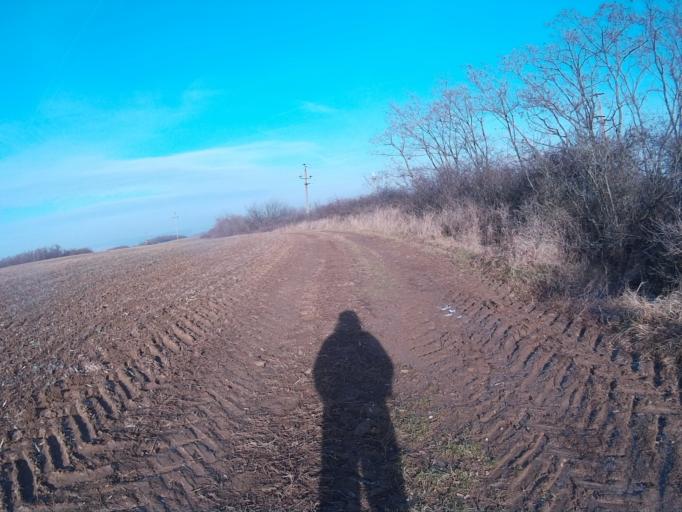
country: HU
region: Nograd
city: Bercel
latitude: 47.9347
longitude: 19.4287
